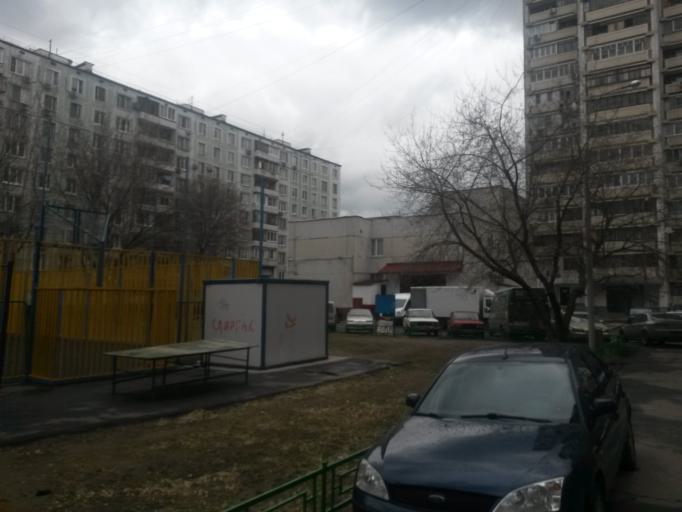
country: RU
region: Moscow
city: Mar'ino
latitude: 55.6452
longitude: 37.7187
